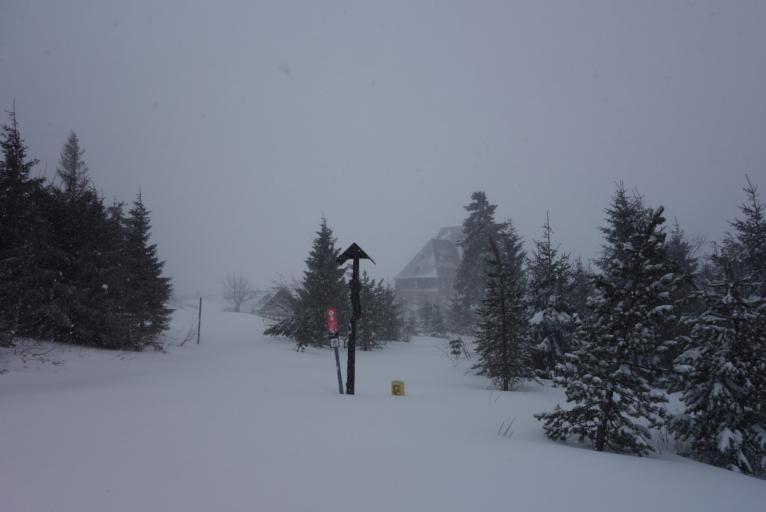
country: DE
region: Saxony
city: Kurort Oberwiesenthal
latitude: 50.4199
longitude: 12.9410
